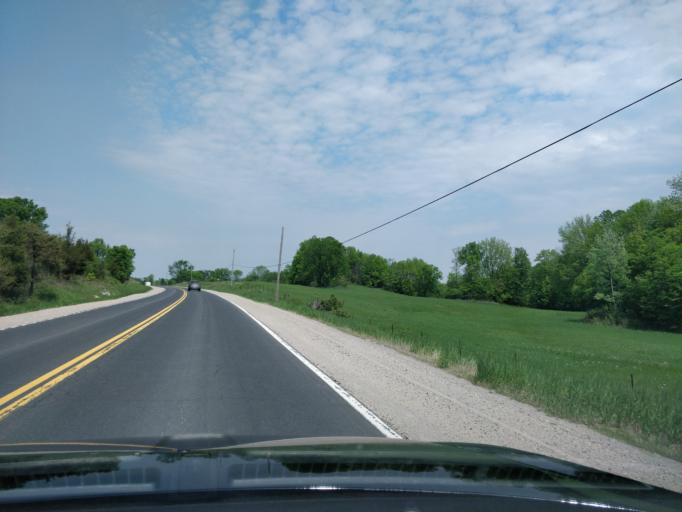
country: CA
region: Ontario
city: Perth
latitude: 44.7708
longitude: -76.3654
